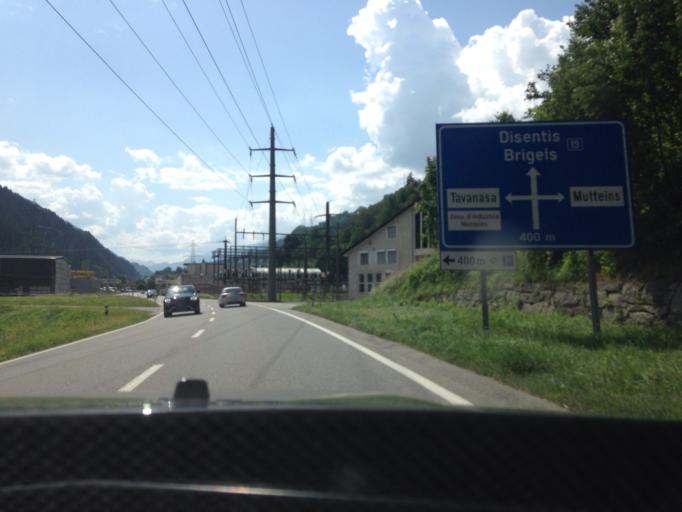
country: CH
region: Grisons
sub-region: Surselva District
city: Breil
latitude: 46.7580
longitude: 9.0729
